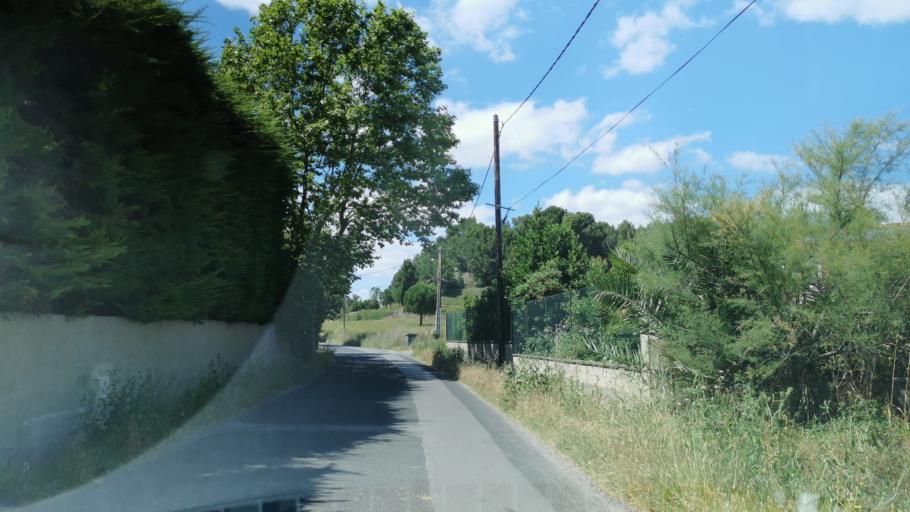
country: FR
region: Languedoc-Roussillon
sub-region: Departement de l'Aude
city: Moussan
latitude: 43.2344
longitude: 2.9451
